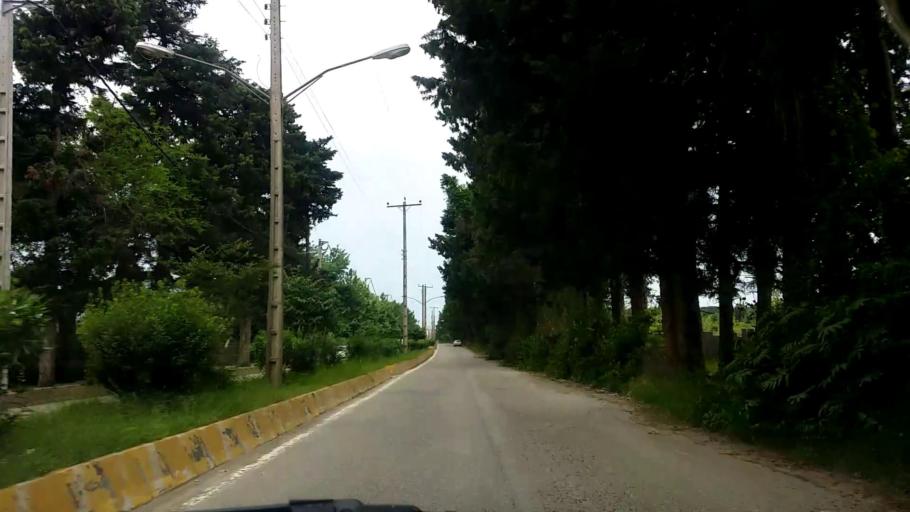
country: IR
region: Mazandaran
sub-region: Nowshahr
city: Nowshahr
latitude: 36.6319
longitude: 51.5027
